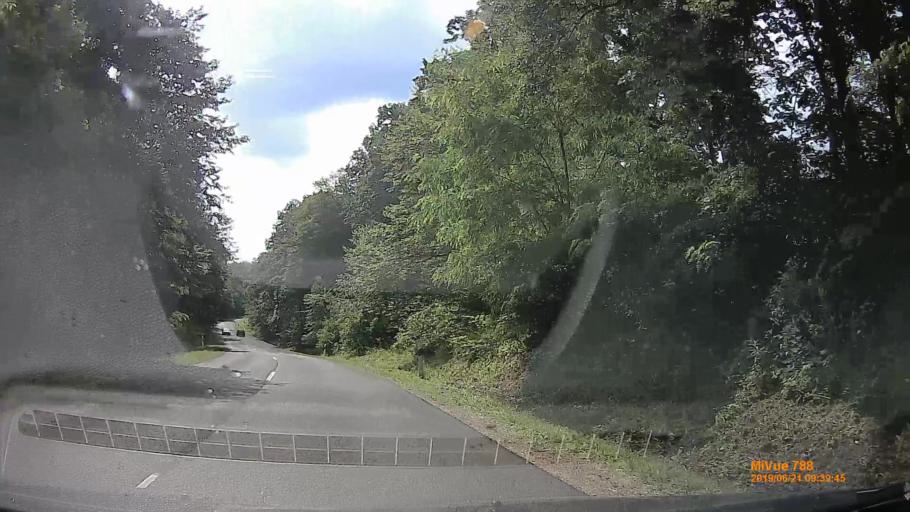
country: HU
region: Somogy
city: Taszar
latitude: 46.2950
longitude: 17.9328
